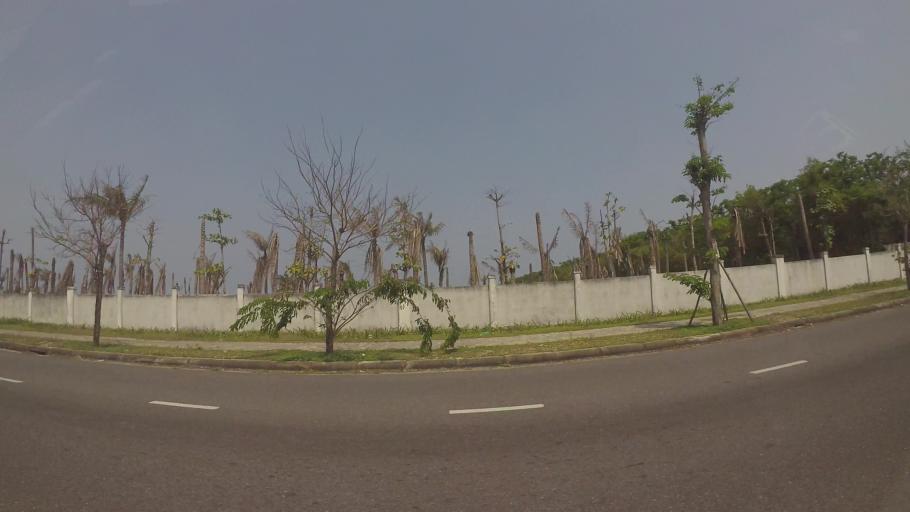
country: VN
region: Da Nang
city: Ngu Hanh Son
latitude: 15.9897
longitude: 108.2710
